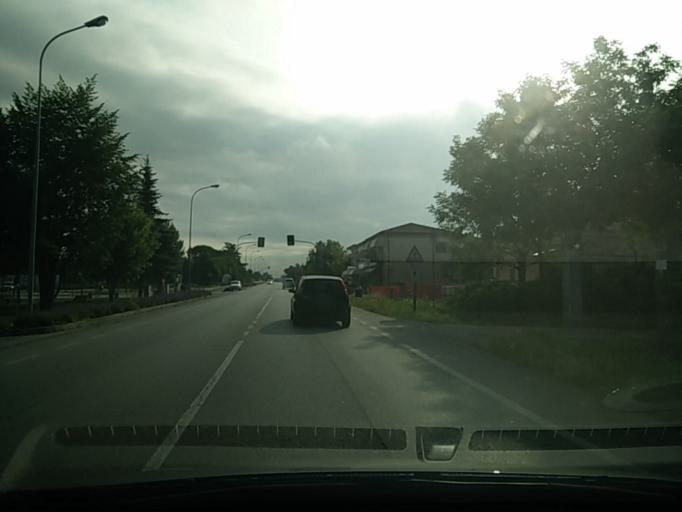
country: IT
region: Veneto
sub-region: Provincia di Venezia
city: San Dona di Piave
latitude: 45.6372
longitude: 12.6071
